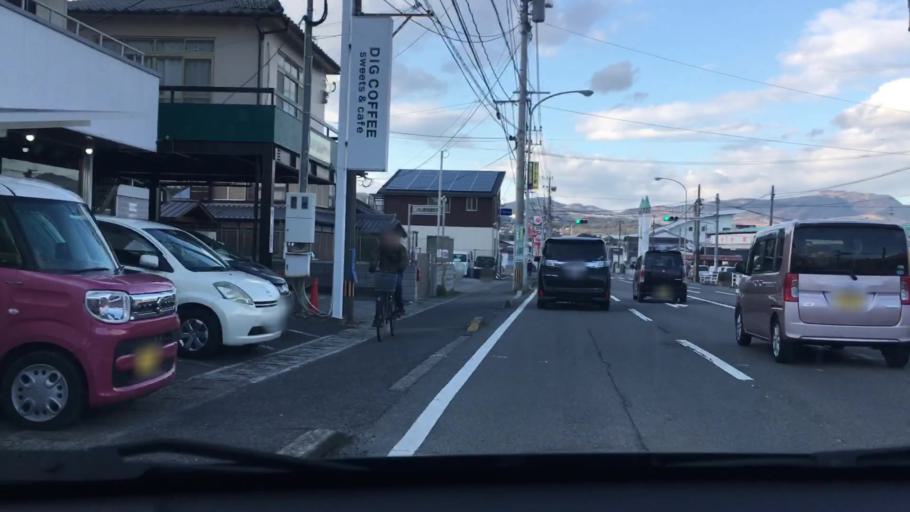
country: JP
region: Oita
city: Beppu
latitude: 33.3198
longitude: 131.4988
